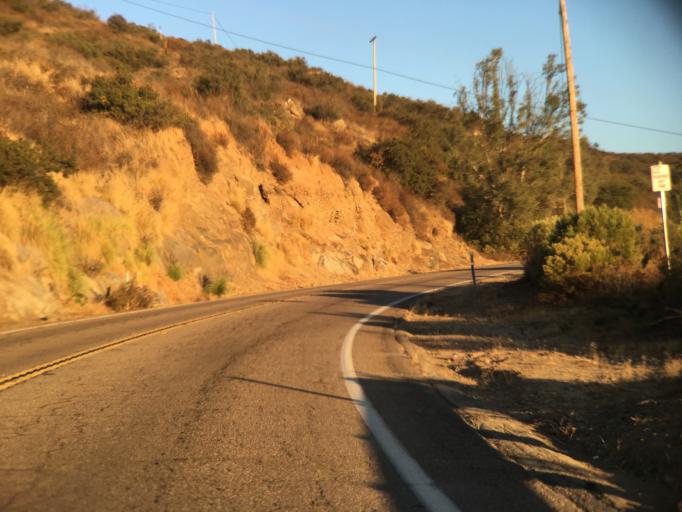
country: US
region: California
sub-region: San Diego County
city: Alpine
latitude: 32.8055
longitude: -116.7819
